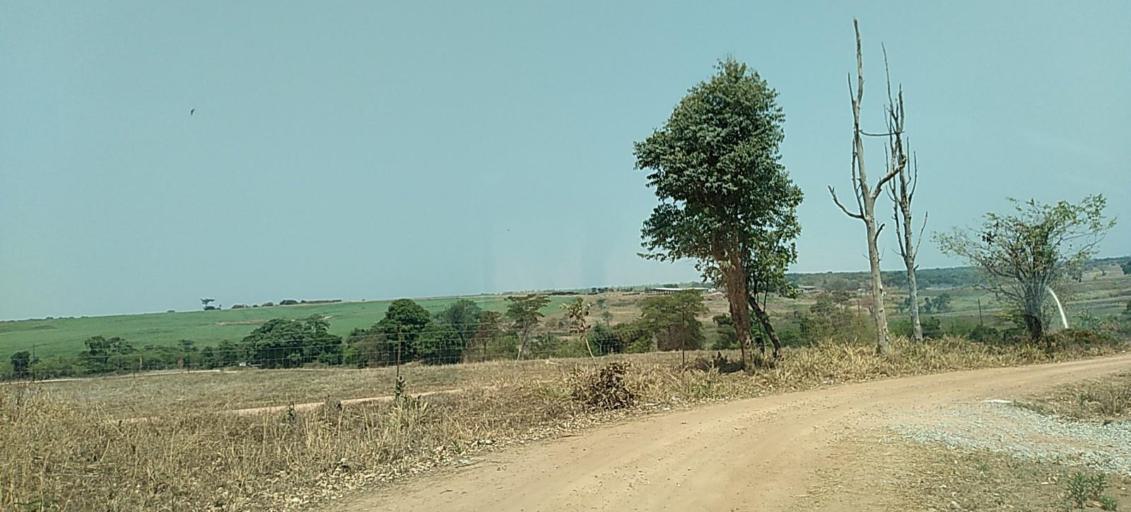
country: ZM
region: Copperbelt
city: Chambishi
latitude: -12.6308
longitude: 27.9435
